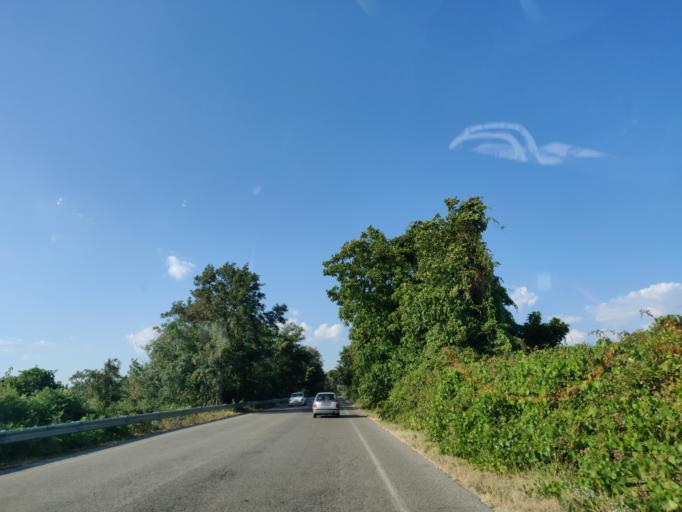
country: IT
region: Latium
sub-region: Provincia di Viterbo
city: Valentano
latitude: 42.5874
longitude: 11.8355
